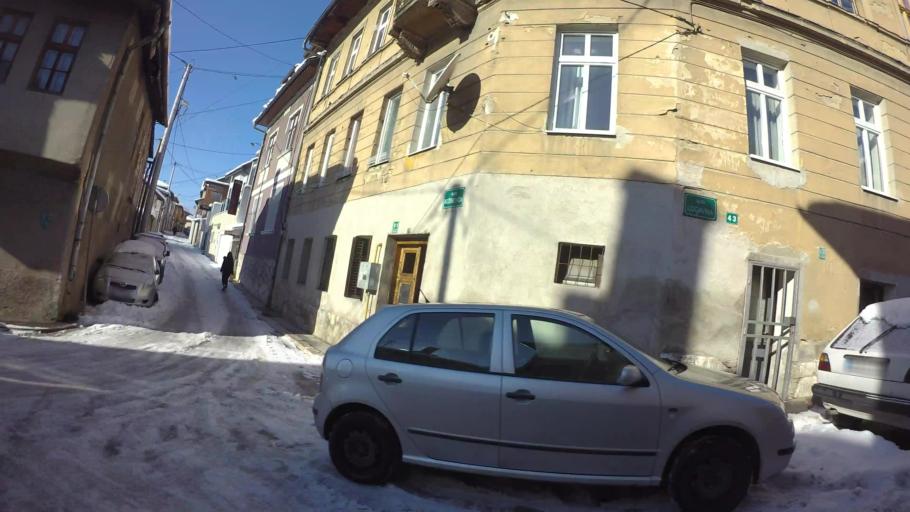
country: BA
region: Federation of Bosnia and Herzegovina
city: Kobilja Glava
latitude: 43.8633
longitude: 18.4280
